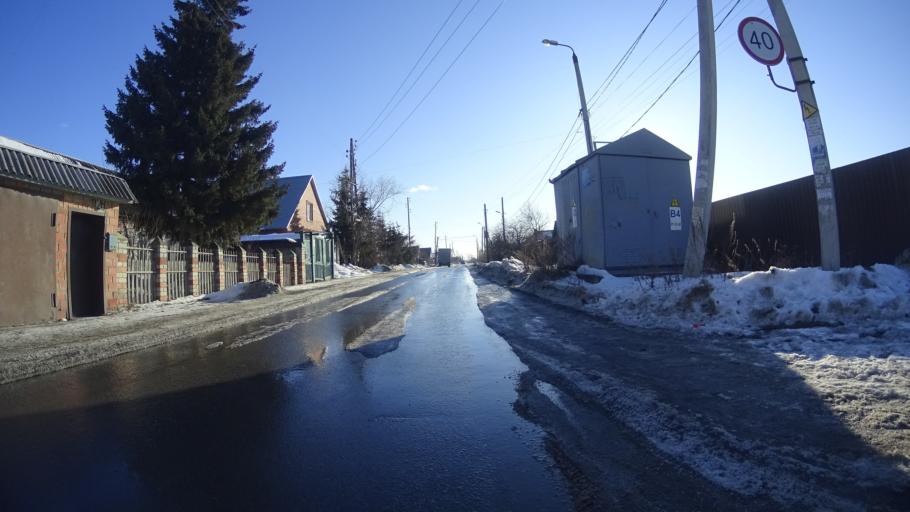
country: RU
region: Chelyabinsk
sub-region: Gorod Chelyabinsk
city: Chelyabinsk
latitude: 55.1530
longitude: 61.3099
